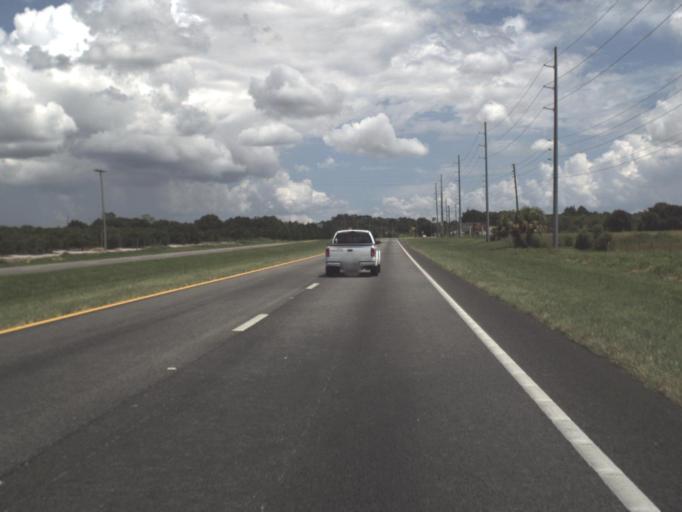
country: US
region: Florida
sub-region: Polk County
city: Lake Wales
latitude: 27.9014
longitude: -81.6360
